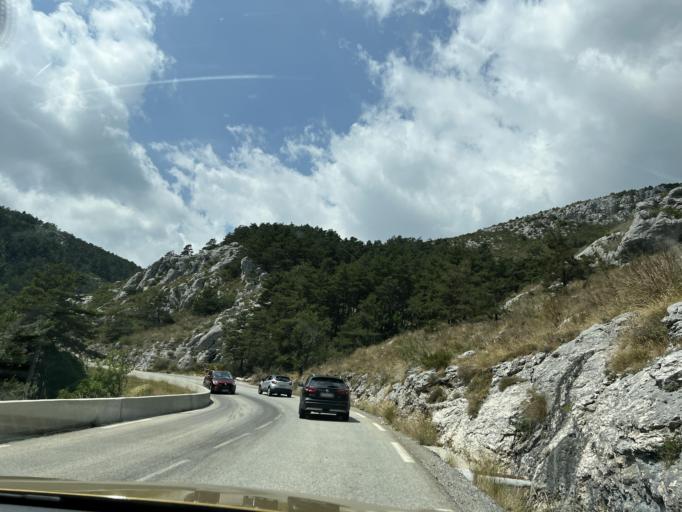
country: FR
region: Provence-Alpes-Cote d'Azur
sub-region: Departement des Alpes-Maritimes
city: Saint-Vallier-de-Thiey
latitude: 43.8015
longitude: 6.9072
